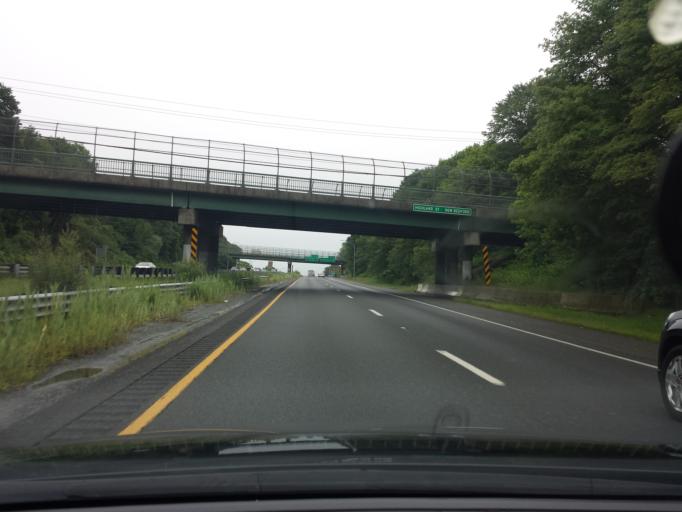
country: US
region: Massachusetts
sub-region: Bristol County
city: New Bedford
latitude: 41.6528
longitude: -70.9398
